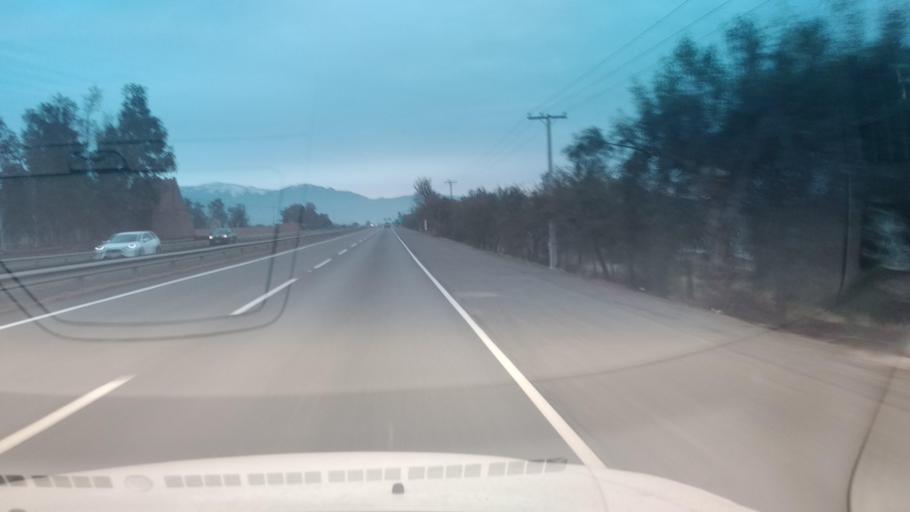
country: CL
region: Santiago Metropolitan
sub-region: Provincia de Chacabuco
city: Chicureo Abajo
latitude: -33.1385
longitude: -70.6643
